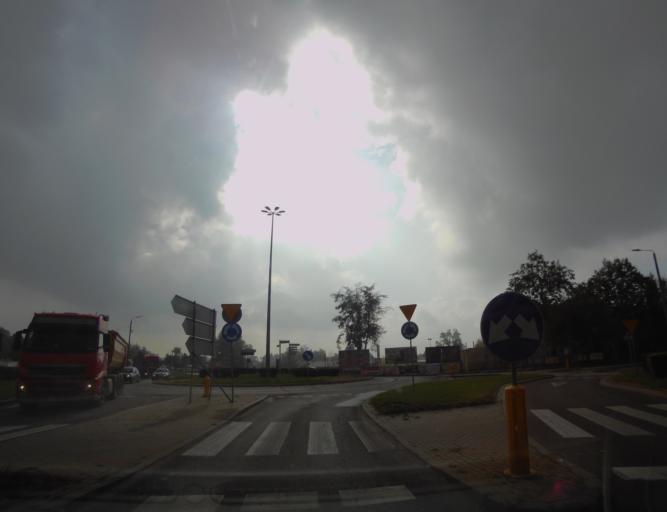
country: PL
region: Lublin Voivodeship
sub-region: Powiat krasnostawski
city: Krasnystaw
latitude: 50.9859
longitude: 23.1818
